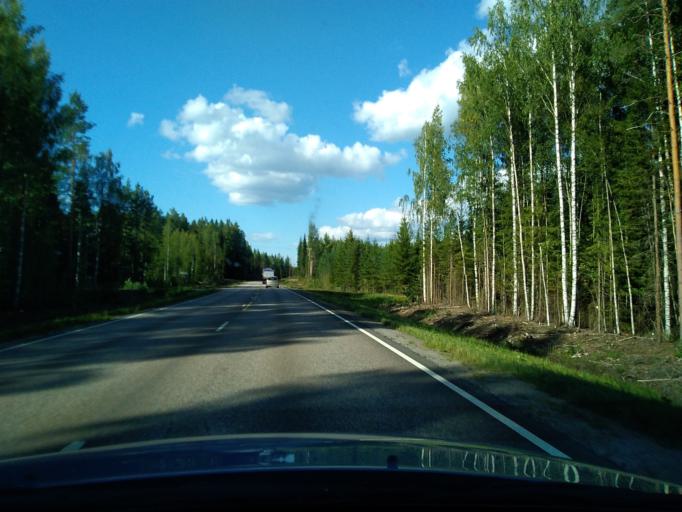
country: FI
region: Pirkanmaa
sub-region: Ylae-Pirkanmaa
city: Maenttae
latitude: 62.1070
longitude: 24.7385
